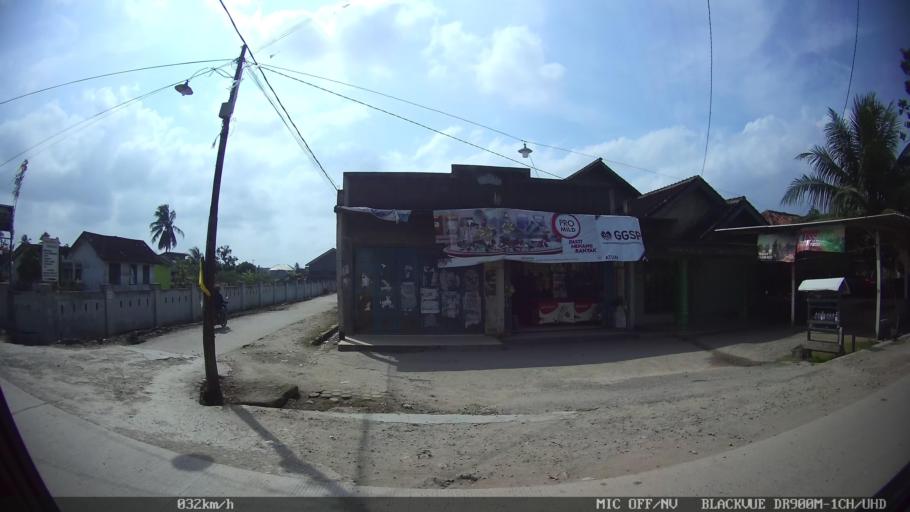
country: ID
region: Lampung
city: Kedaton
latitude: -5.3498
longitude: 105.2653
